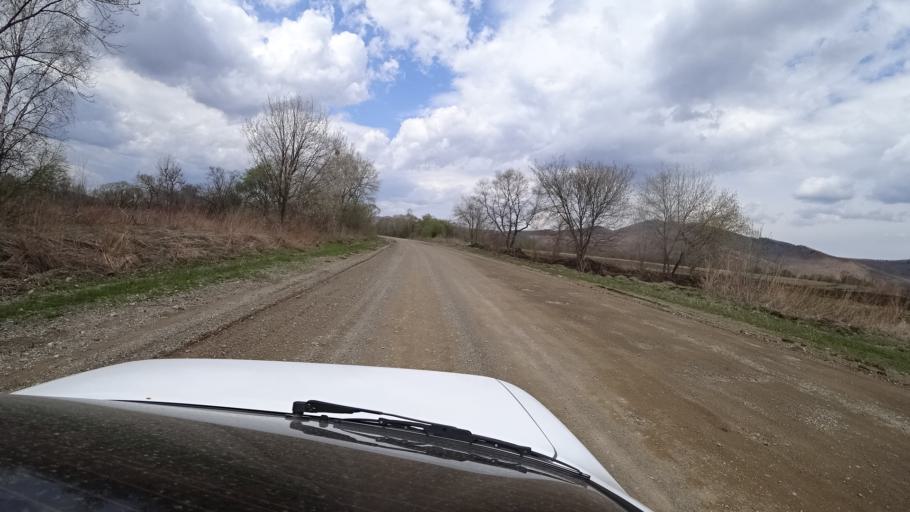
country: RU
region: Primorskiy
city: Novopokrovka
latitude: 45.6131
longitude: 134.2743
